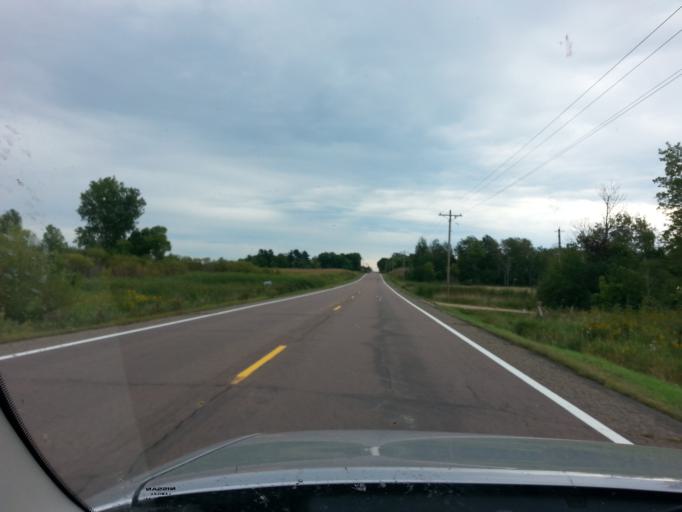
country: US
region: Minnesota
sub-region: Dakota County
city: Farmington
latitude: 44.6305
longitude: -93.1016
